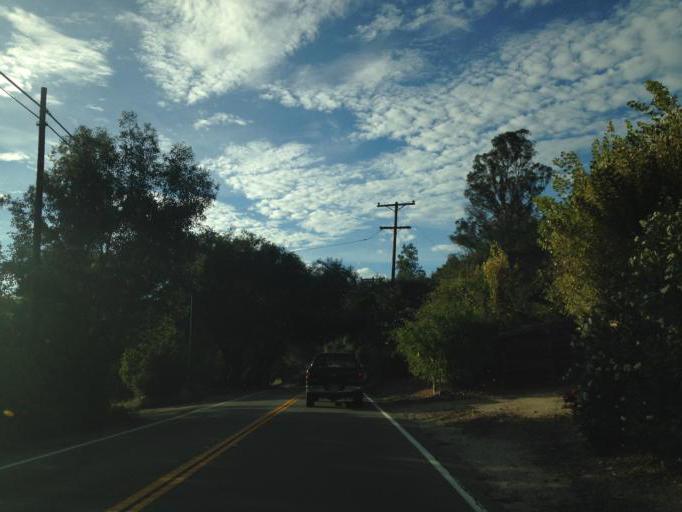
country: US
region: California
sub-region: San Diego County
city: Rainbow
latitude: 33.4163
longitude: -117.0870
